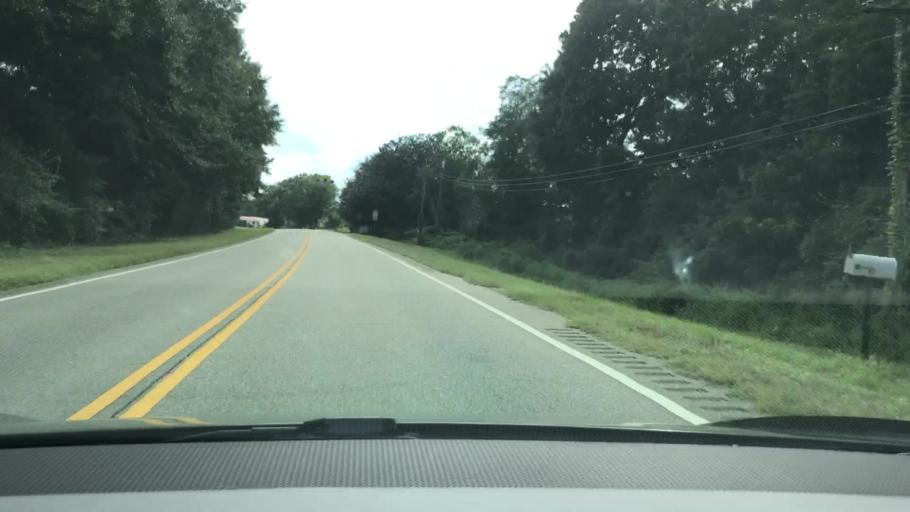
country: US
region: Alabama
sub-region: Coffee County
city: Elba
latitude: 31.5709
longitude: -86.0066
